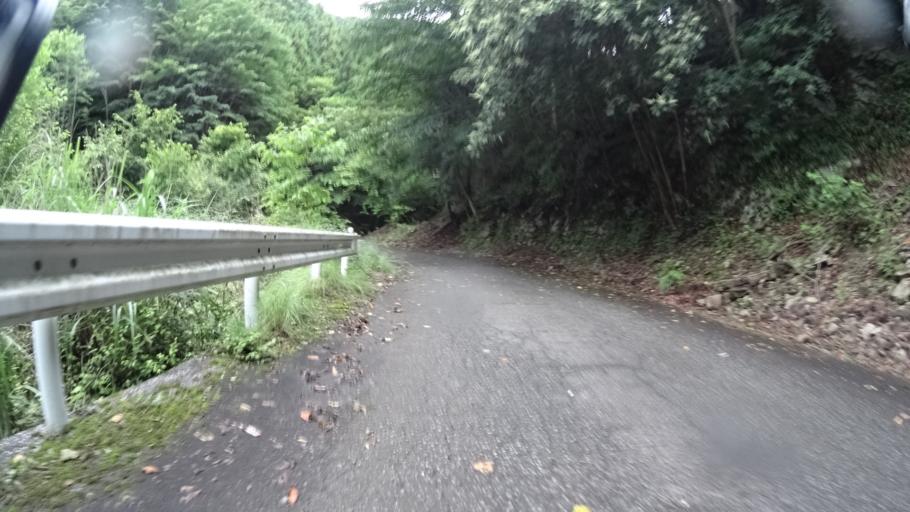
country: JP
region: Saitama
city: Chichibu
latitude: 35.8872
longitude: 139.1201
